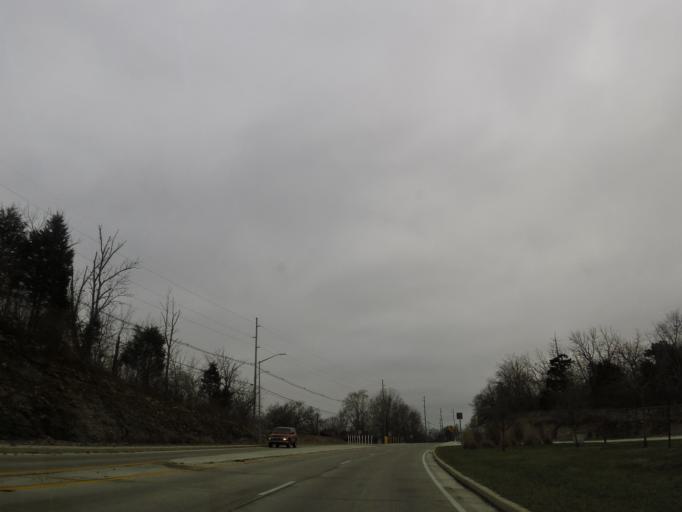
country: US
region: Kentucky
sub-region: Franklin County
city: Frankfort
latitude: 38.1855
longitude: -84.8814
